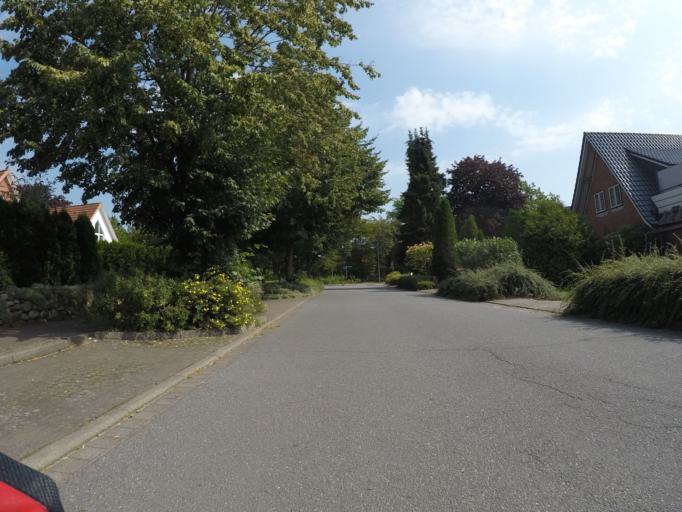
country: DE
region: Schleswig-Holstein
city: Kisdorf
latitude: 53.8059
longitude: 10.0120
